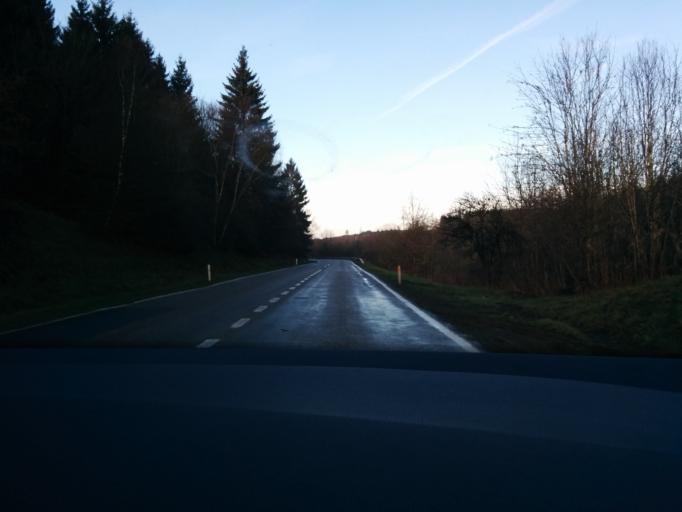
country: BE
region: Wallonia
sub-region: Province du Luxembourg
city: Gouvy
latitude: 50.2188
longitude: 5.9500
